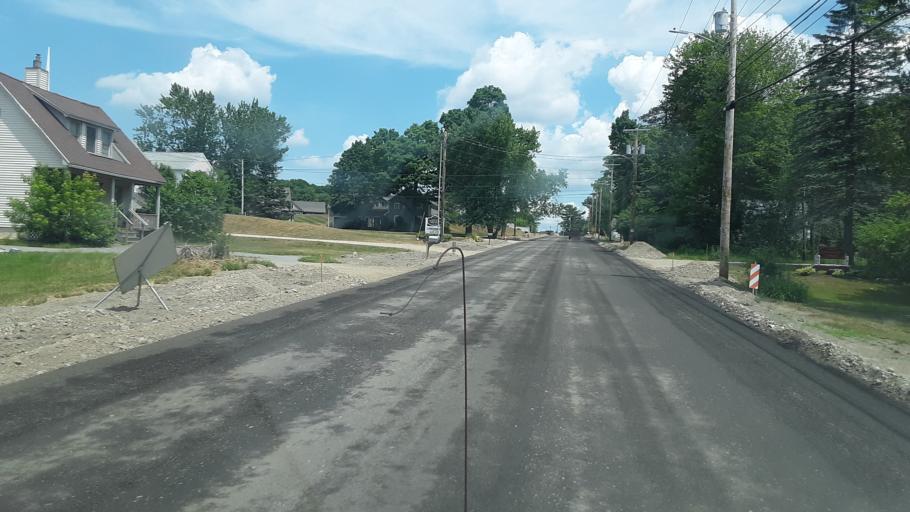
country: US
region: Maine
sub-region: Penobscot County
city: Hampden
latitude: 44.7534
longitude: -68.8241
